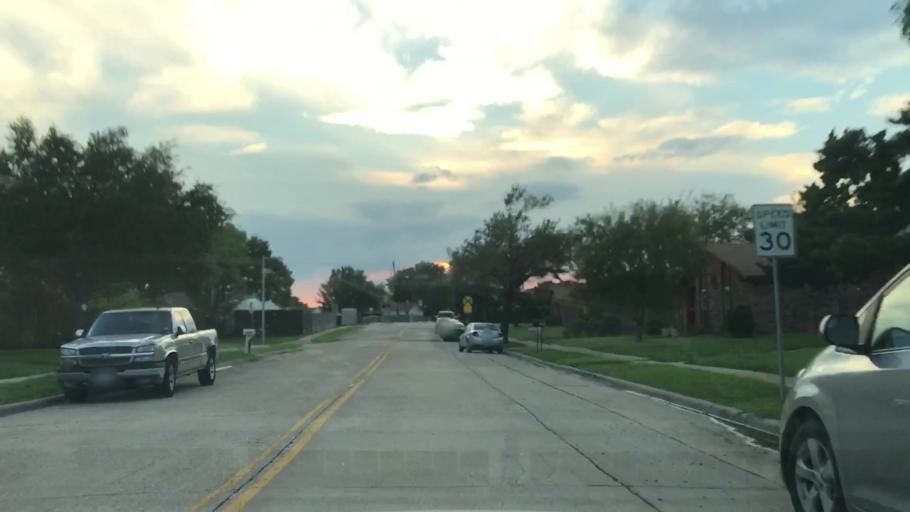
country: US
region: Texas
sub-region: Dallas County
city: Carrollton
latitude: 33.0050
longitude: -96.8692
